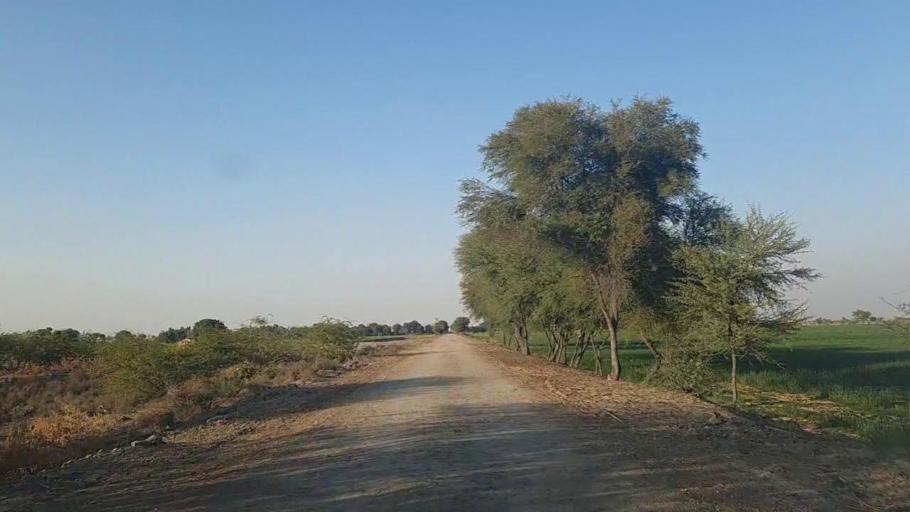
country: PK
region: Sindh
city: Jam Sahib
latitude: 26.3023
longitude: 68.6704
